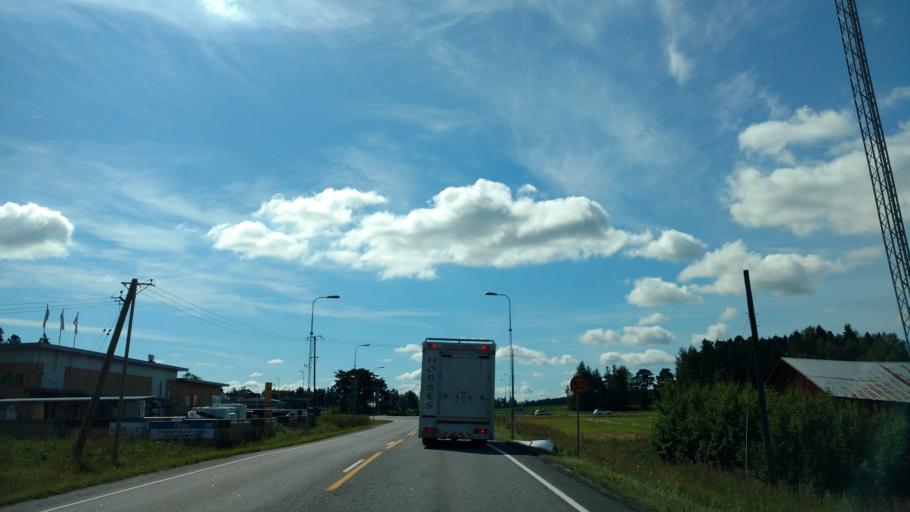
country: FI
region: Varsinais-Suomi
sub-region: Salo
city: Pernioe
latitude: 60.2071
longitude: 23.1112
